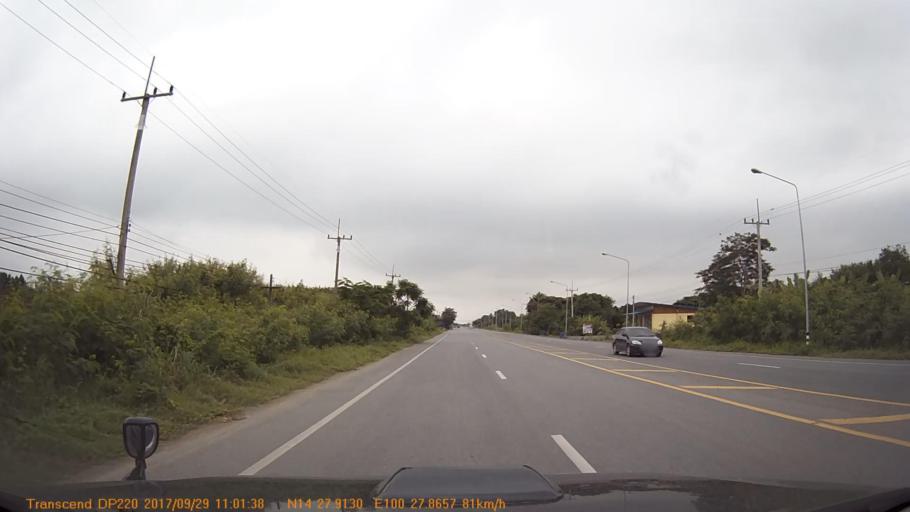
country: TH
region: Ang Thong
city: Pa Mok
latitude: 14.4655
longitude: 100.4642
